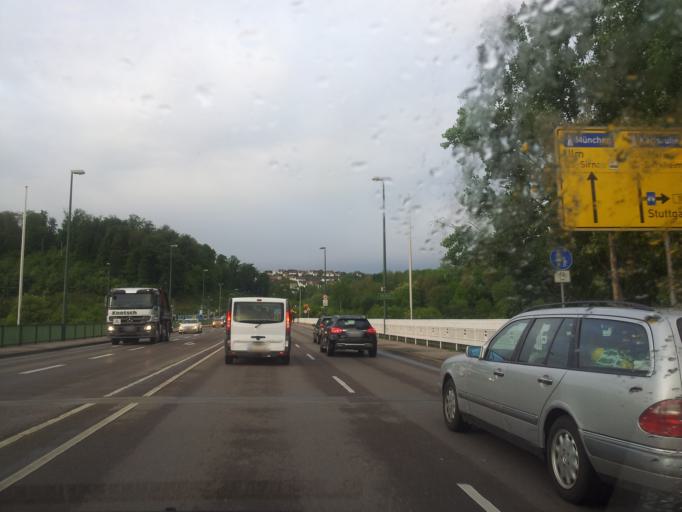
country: DE
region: Baden-Wuerttemberg
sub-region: Regierungsbezirk Stuttgart
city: Esslingen
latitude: 48.7290
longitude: 9.3208
